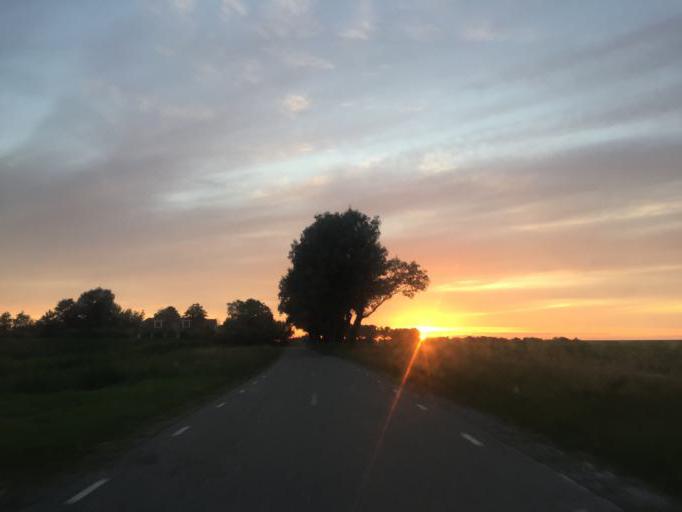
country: NL
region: Friesland
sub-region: Gemeente Dongeradeel
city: Anjum
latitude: 53.3884
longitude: 6.1081
